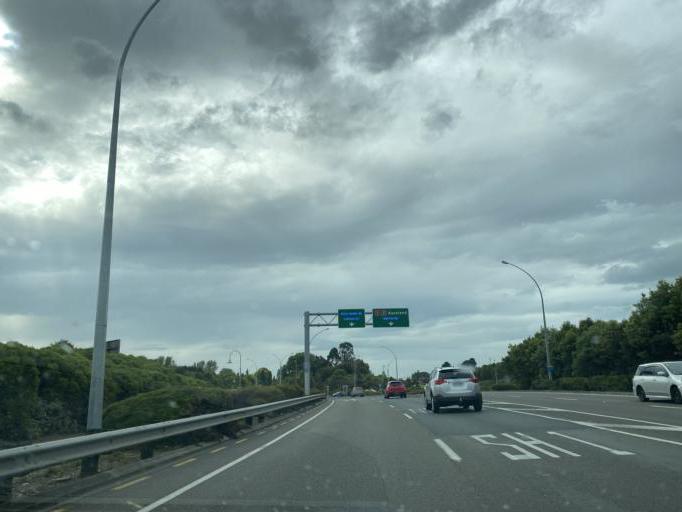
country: NZ
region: Waikato
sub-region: Hamilton City
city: Hamilton
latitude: -37.7839
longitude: 175.2542
